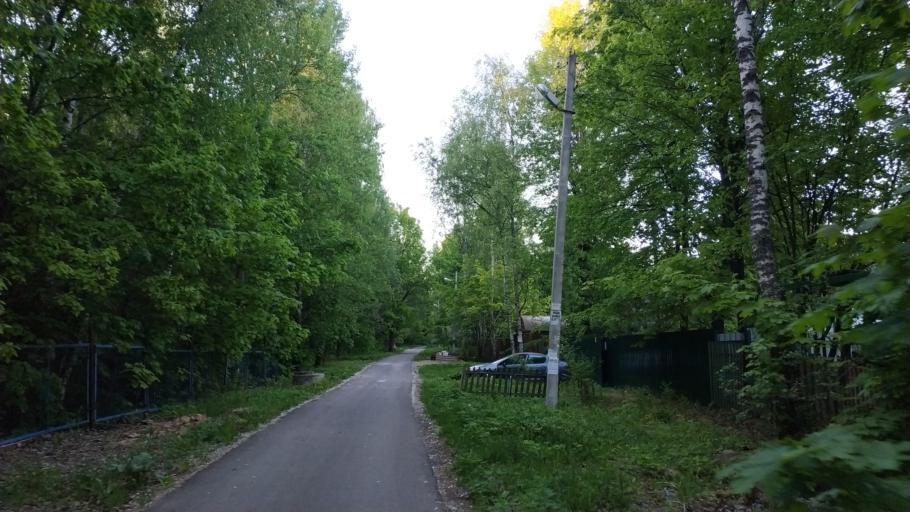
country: RU
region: Moskovskaya
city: Zelenogradskiy
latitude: 56.1152
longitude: 37.9194
